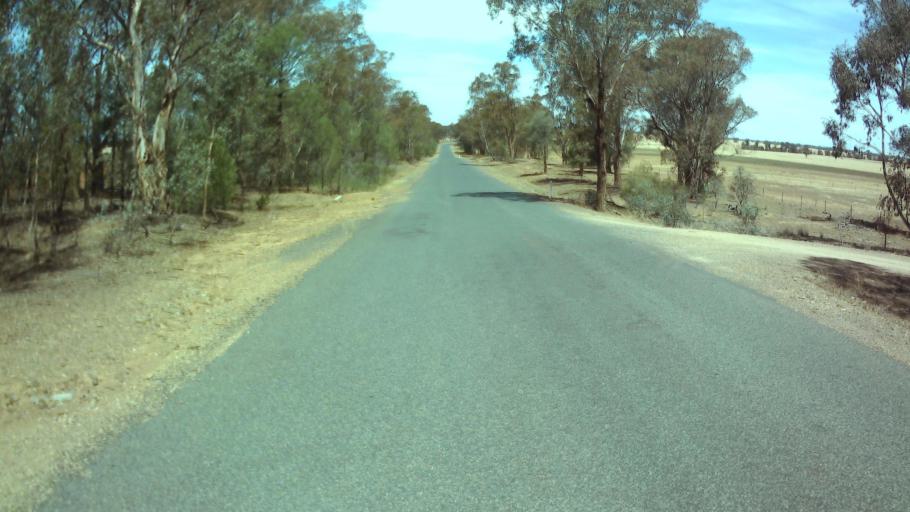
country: AU
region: New South Wales
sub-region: Weddin
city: Grenfell
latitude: -33.9038
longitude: 147.7592
